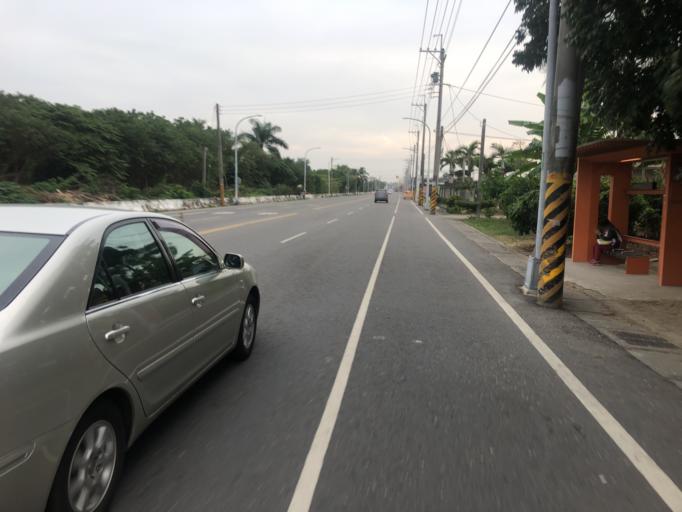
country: TW
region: Taiwan
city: Xinying
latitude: 23.1472
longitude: 120.2880
